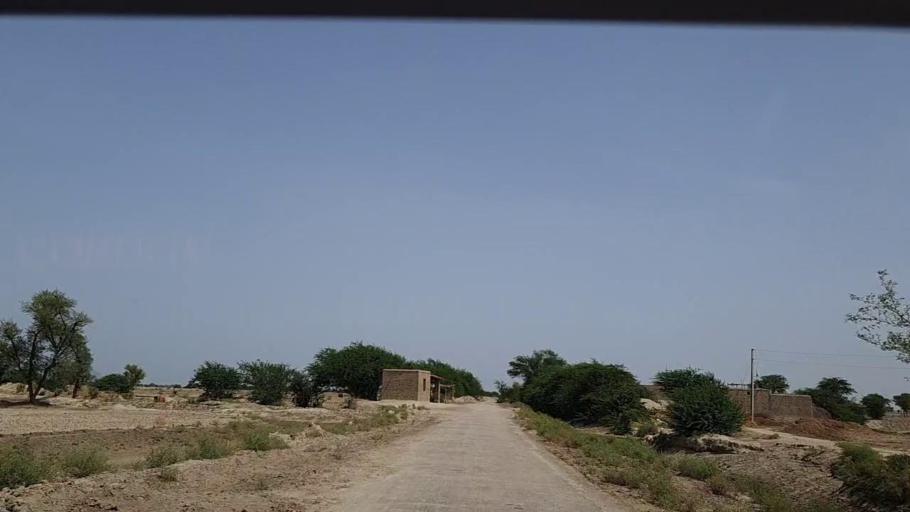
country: PK
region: Sindh
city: Johi
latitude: 26.7739
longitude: 67.6256
